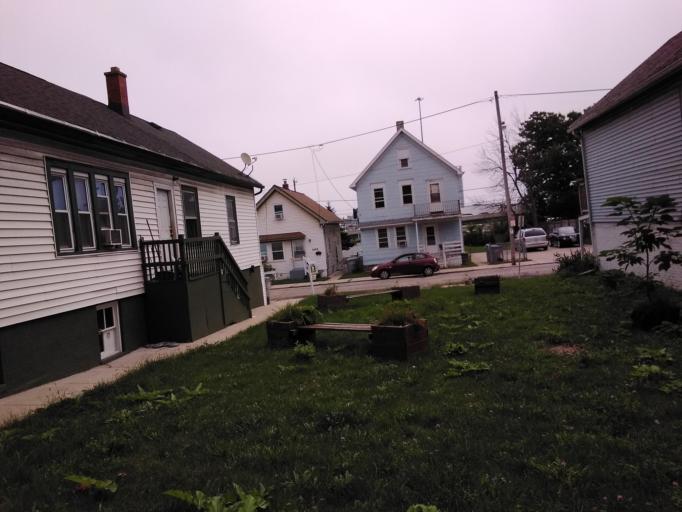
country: US
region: Wisconsin
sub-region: Milwaukee County
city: Milwaukee
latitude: 43.0075
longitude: -87.9181
